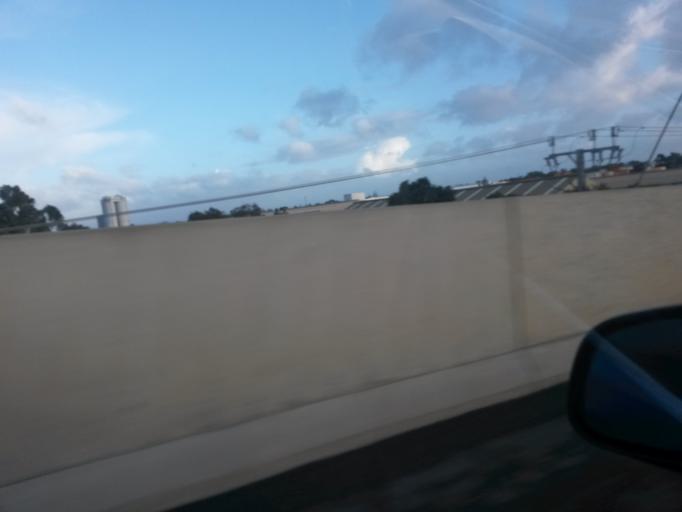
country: AU
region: South Australia
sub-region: Port Adelaide Enfield
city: Alberton
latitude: -34.8391
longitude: 138.5210
